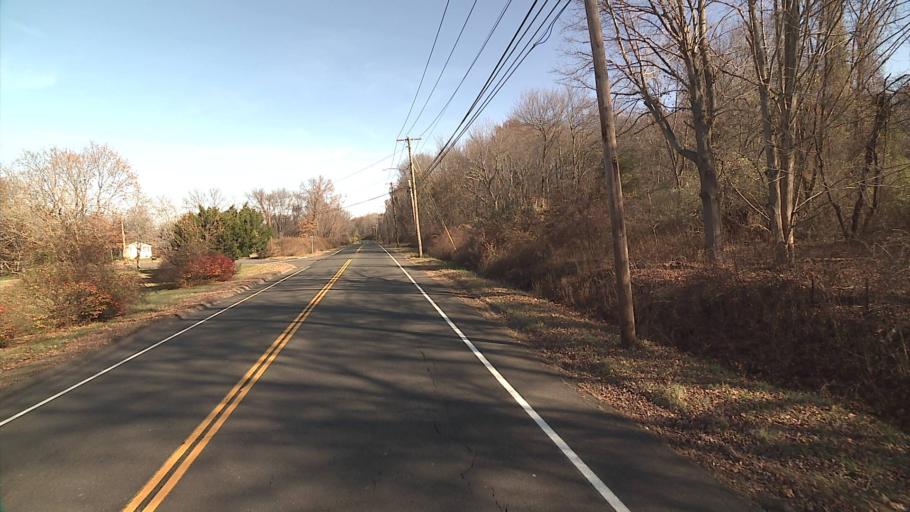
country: US
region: Connecticut
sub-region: New Haven County
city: North Haven
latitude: 41.3445
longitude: -72.8582
